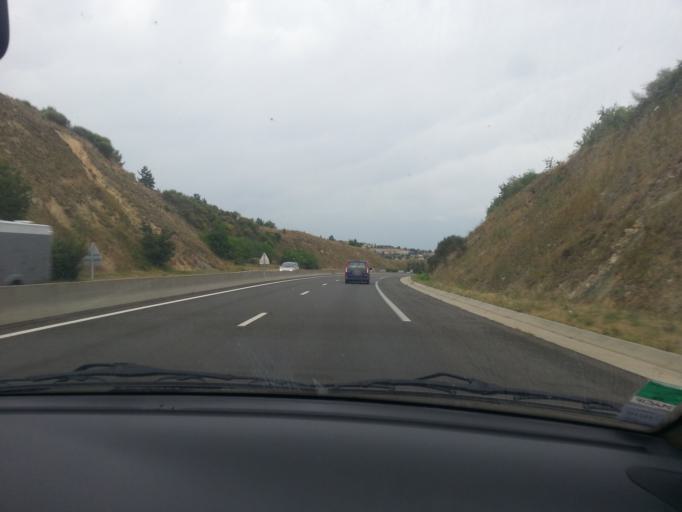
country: FR
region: Languedoc-Roussillon
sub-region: Departement de la Lozere
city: Chirac
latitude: 44.5226
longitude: 3.2408
